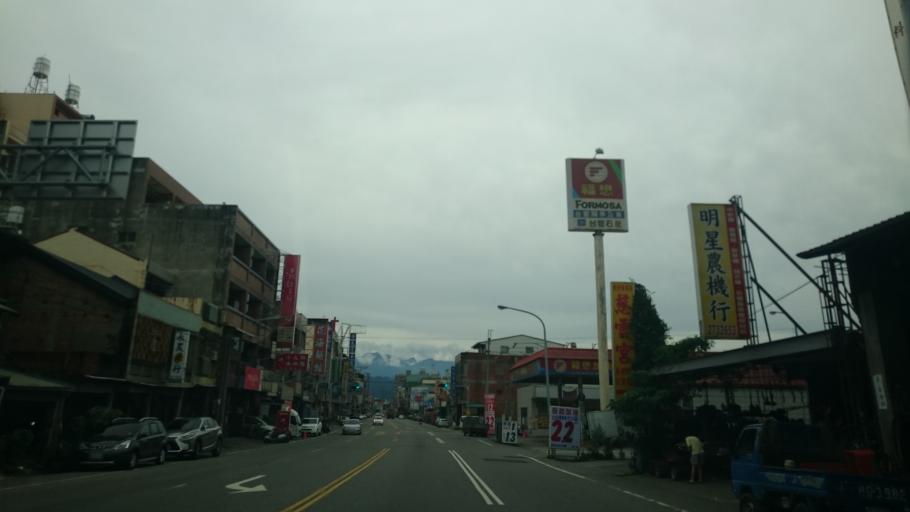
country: TW
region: Taiwan
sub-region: Nantou
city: Nantou
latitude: 23.8422
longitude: 120.6999
